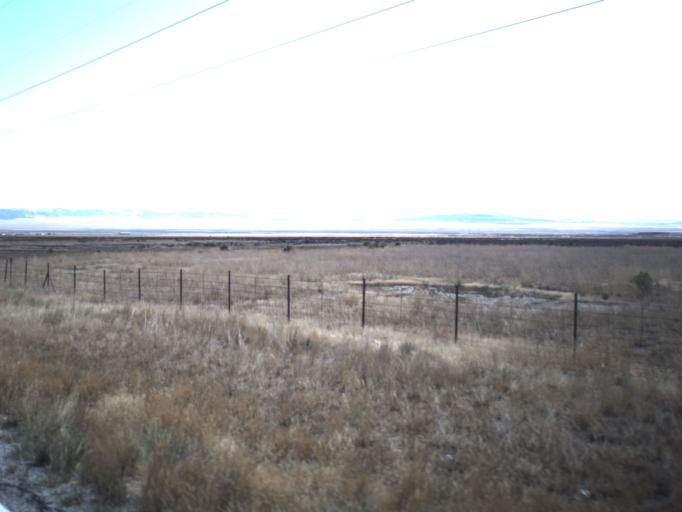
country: US
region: Idaho
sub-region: Oneida County
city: Malad City
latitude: 41.9655
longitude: -113.0281
